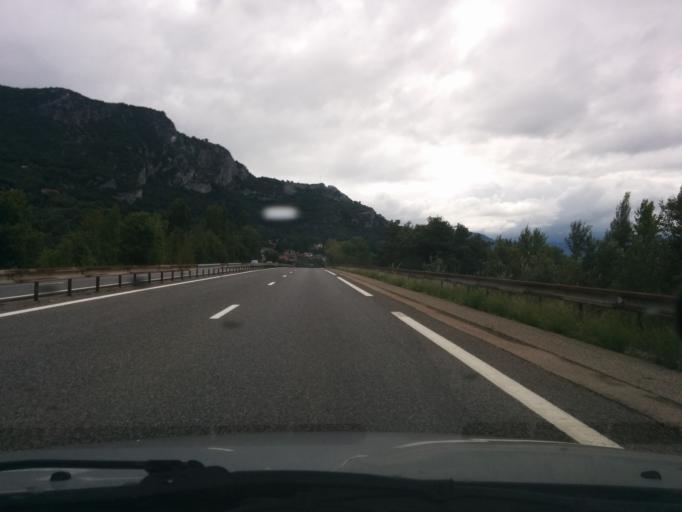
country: FR
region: Rhone-Alpes
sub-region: Departement de l'Isere
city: Saint-Martin-le-Vinoux
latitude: 45.2077
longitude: 5.7041
